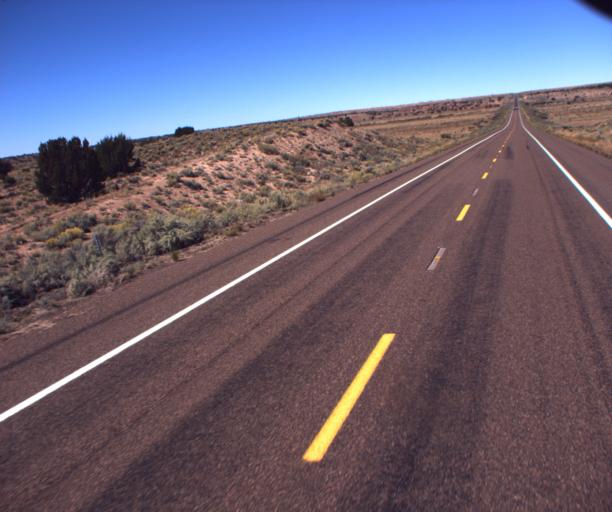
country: US
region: Arizona
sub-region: Apache County
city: Saint Johns
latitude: 34.6617
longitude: -109.7162
